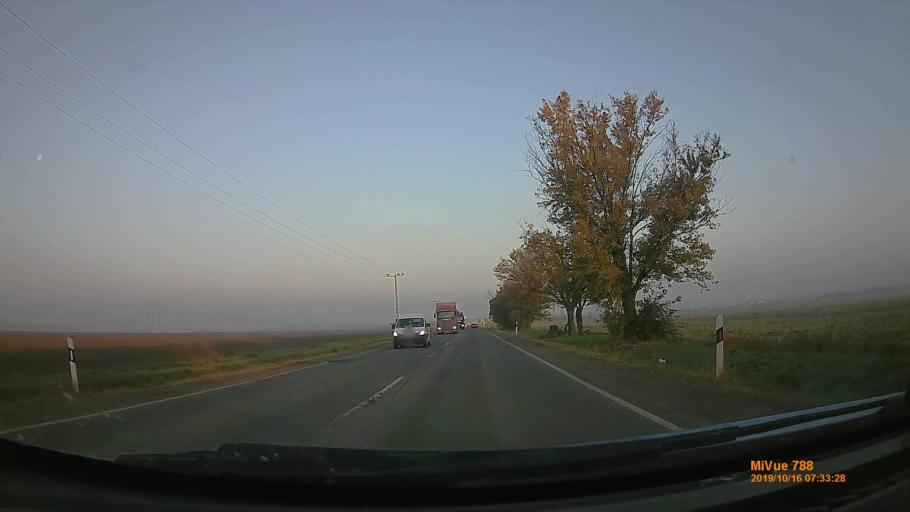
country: HU
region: Heves
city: Fuzesabony
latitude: 47.7701
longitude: 20.3820
